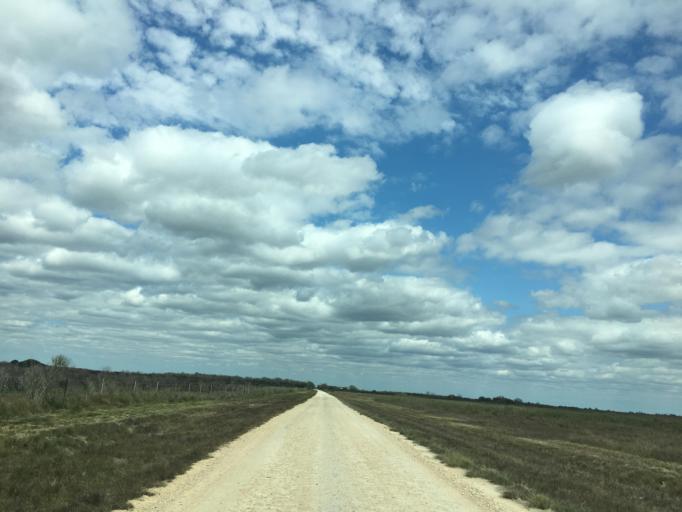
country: US
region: Texas
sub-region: Brazoria County
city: Oyster Creek
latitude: 29.0485
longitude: -95.2684
